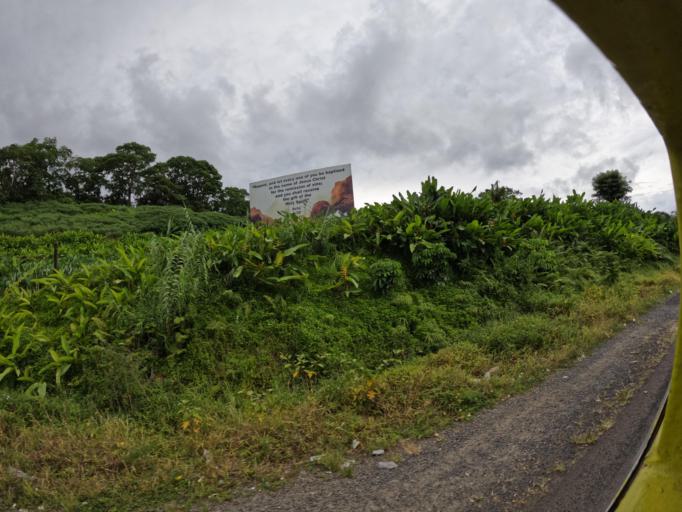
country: FJ
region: Central
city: Suva
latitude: -18.0702
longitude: 178.4610
